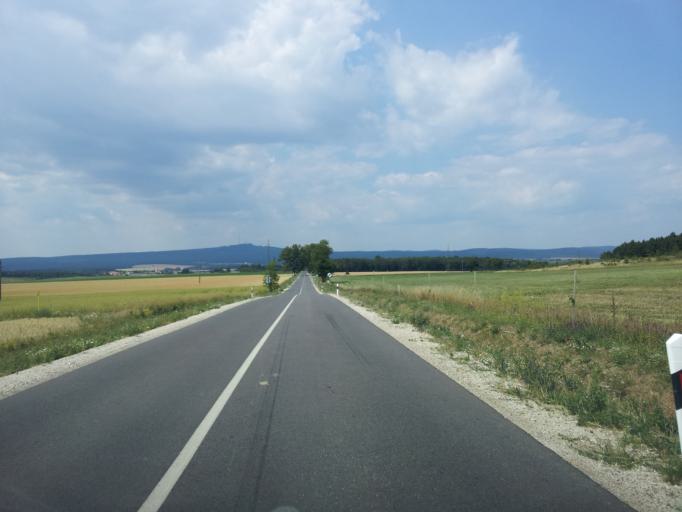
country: HU
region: Veszprem
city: Zanka
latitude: 46.9575
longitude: 17.7016
